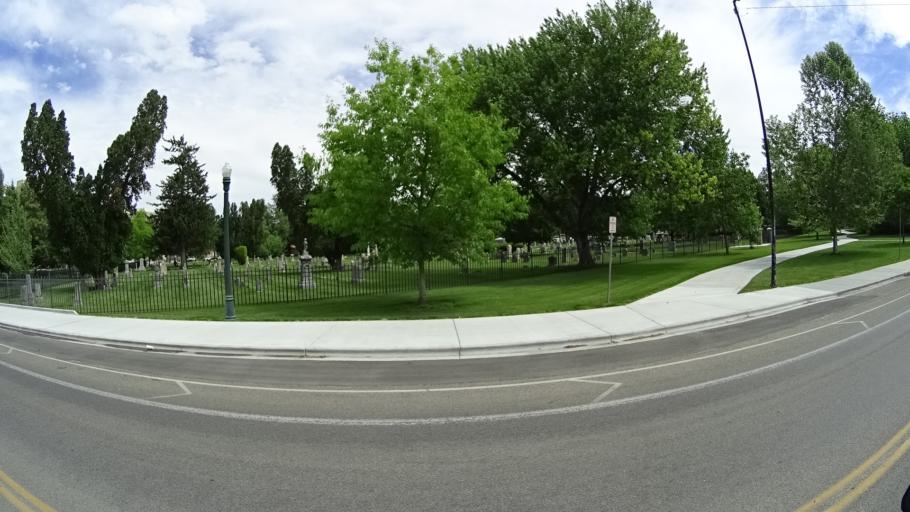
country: US
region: Idaho
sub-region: Ada County
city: Boise
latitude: 43.6104
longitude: -116.1901
